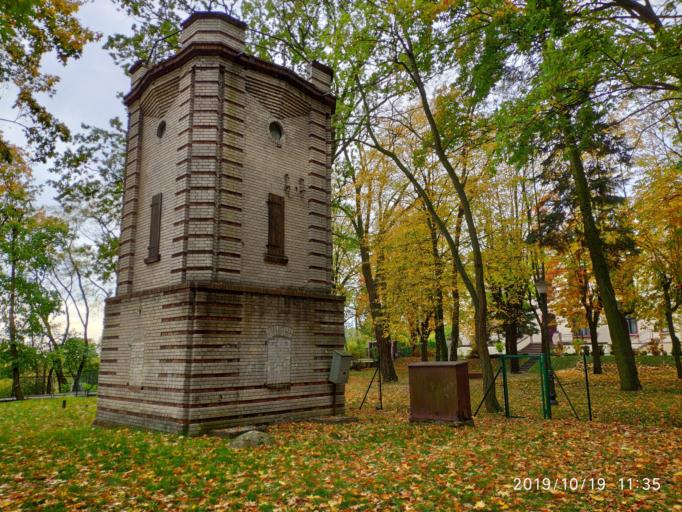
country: PL
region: Lubusz
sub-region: Zielona Gora
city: Zielona Gora
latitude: 51.9267
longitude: 15.4952
